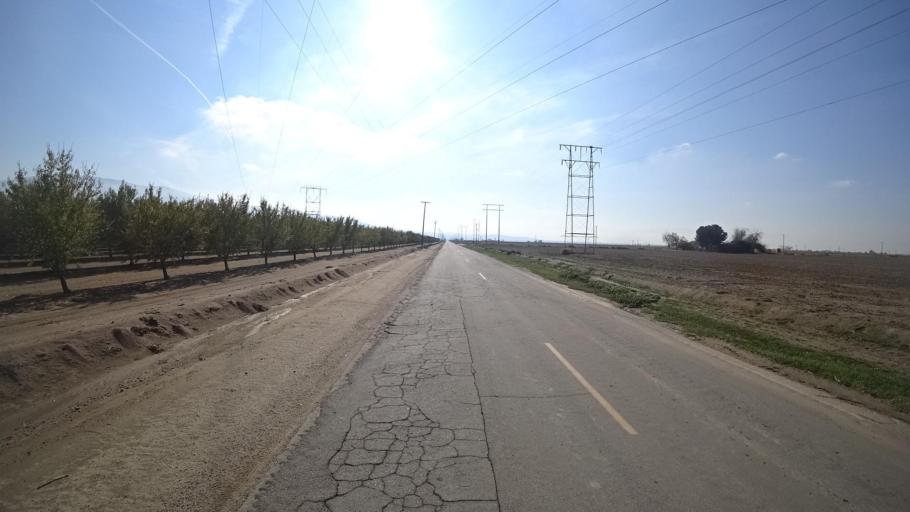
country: US
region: California
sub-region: Kern County
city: Arvin
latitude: 35.2290
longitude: -118.8066
